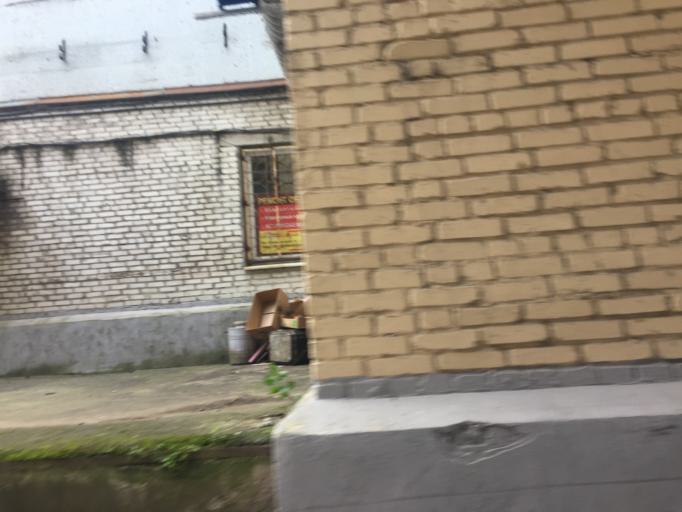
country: RU
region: St.-Petersburg
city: Obukhovo
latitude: 59.8650
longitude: 30.4711
